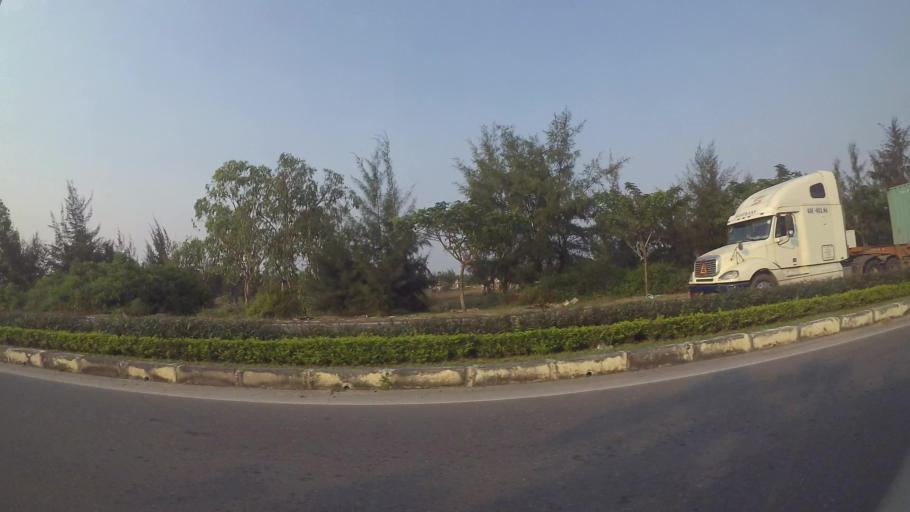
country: VN
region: Da Nang
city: Ngu Hanh Son
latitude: 15.9835
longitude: 108.2436
